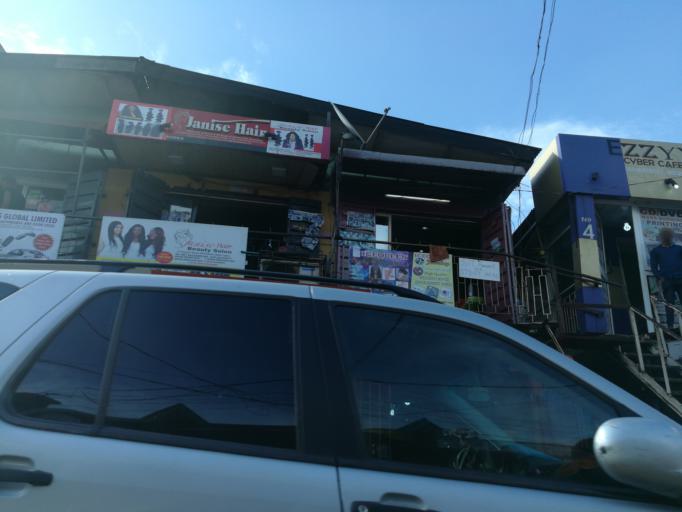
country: NG
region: Lagos
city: Ikeja
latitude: 6.5960
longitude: 3.3422
